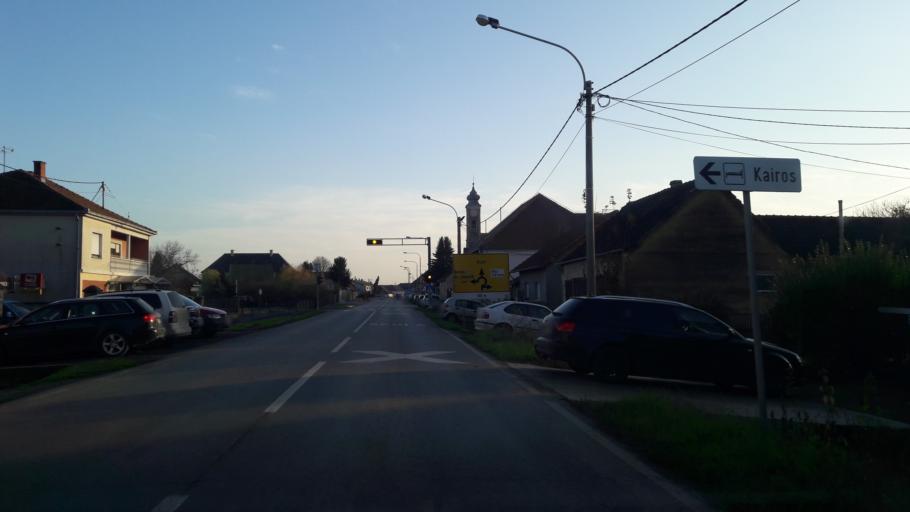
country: HR
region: Osjecko-Baranjska
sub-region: Grad Osijek
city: Bilje
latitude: 45.6059
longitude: 18.7429
